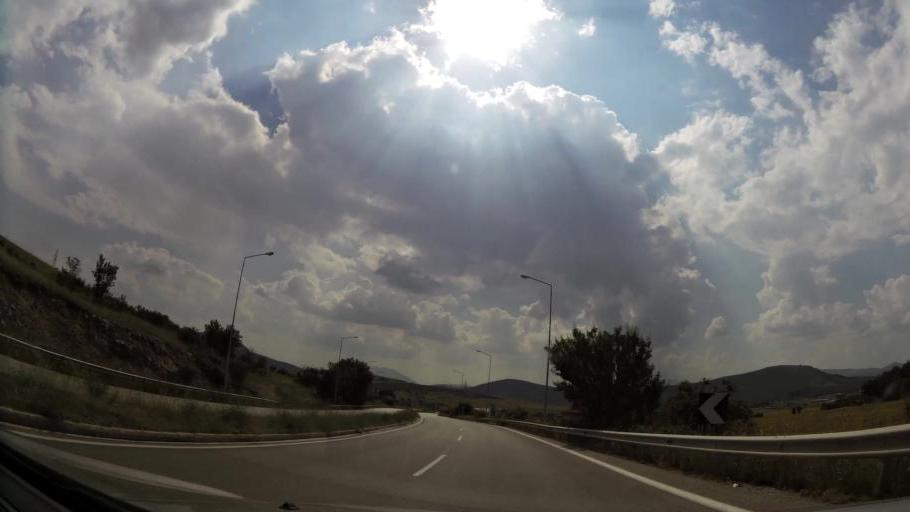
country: GR
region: West Macedonia
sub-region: Nomos Kozanis
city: Koila
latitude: 40.3422
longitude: 21.8161
